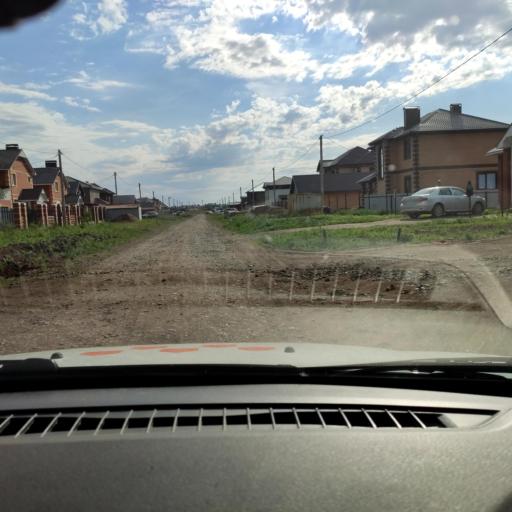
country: RU
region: Bashkortostan
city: Ufa
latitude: 54.6309
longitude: 55.9071
